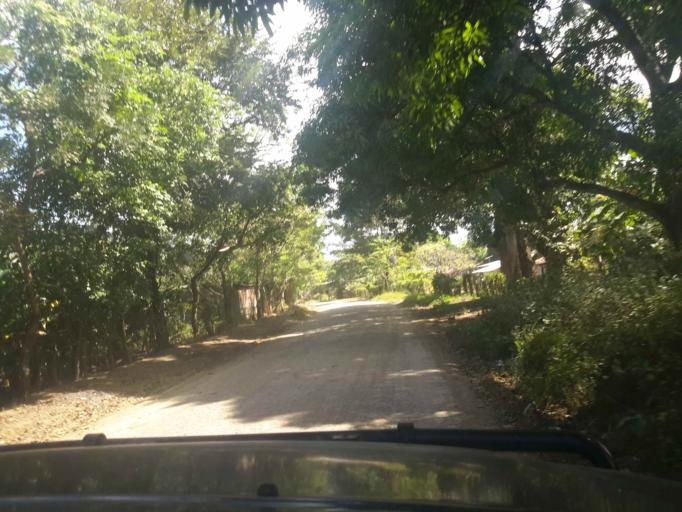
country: NI
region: Granada
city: Nandaime
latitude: 11.6579
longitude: -85.9656
